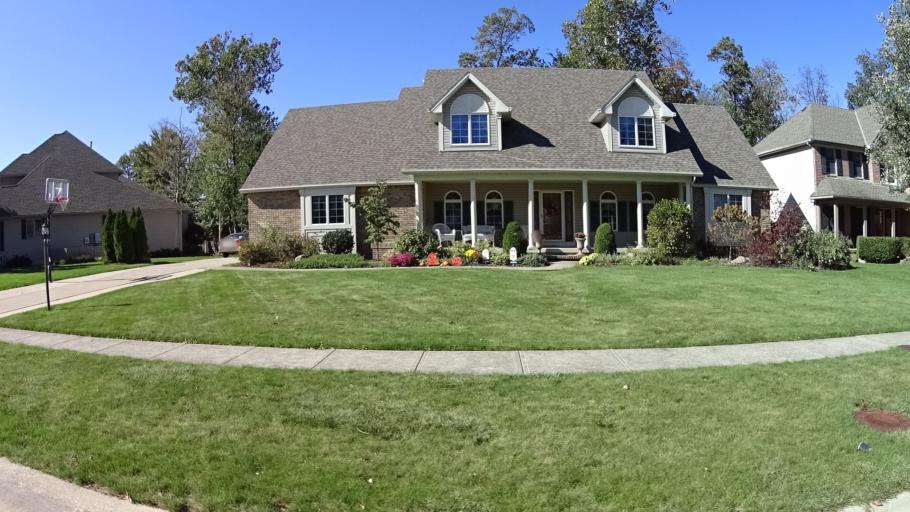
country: US
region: Ohio
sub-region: Lorain County
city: Amherst
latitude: 41.3859
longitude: -82.2263
